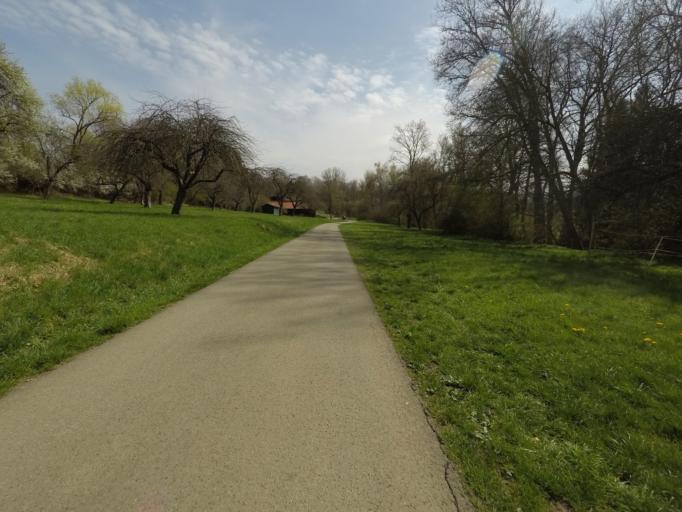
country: DE
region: Baden-Wuerttemberg
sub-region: Tuebingen Region
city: Reutlingen
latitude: 48.4824
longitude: 9.1771
